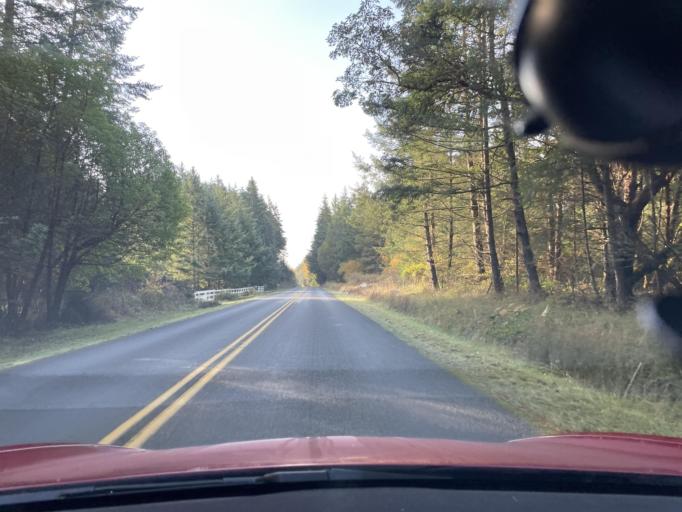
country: US
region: Washington
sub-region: San Juan County
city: Friday Harbor
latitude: 48.5639
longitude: -123.1648
